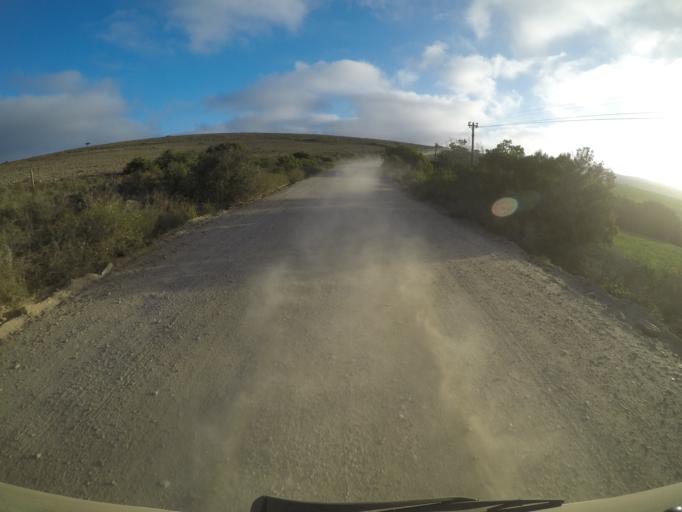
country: ZA
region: Western Cape
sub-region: Eden District Municipality
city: Mossel Bay
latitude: -34.1259
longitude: 22.0515
